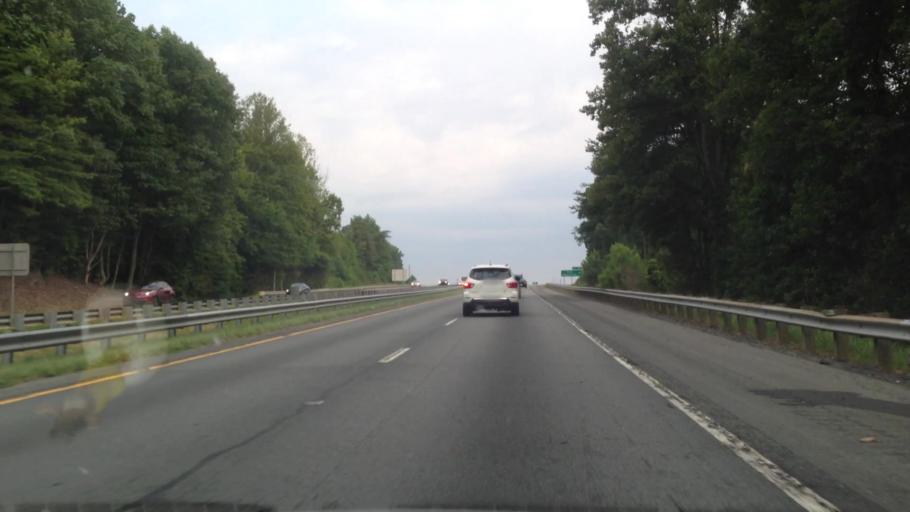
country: US
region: North Carolina
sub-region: Forsyth County
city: Tobaccoville
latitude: 36.2545
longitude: -80.3589
